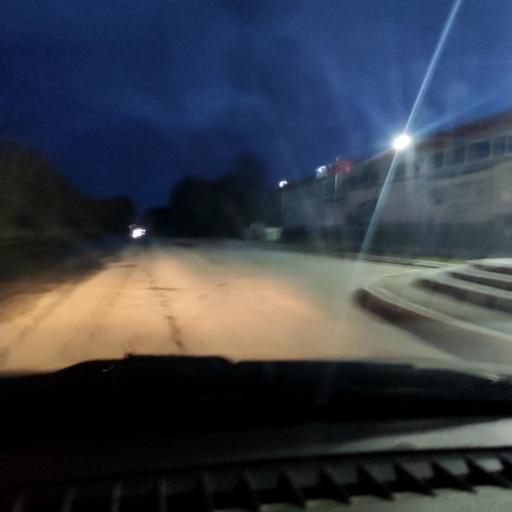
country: RU
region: Samara
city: Tol'yatti
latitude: 53.5724
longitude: 49.2878
